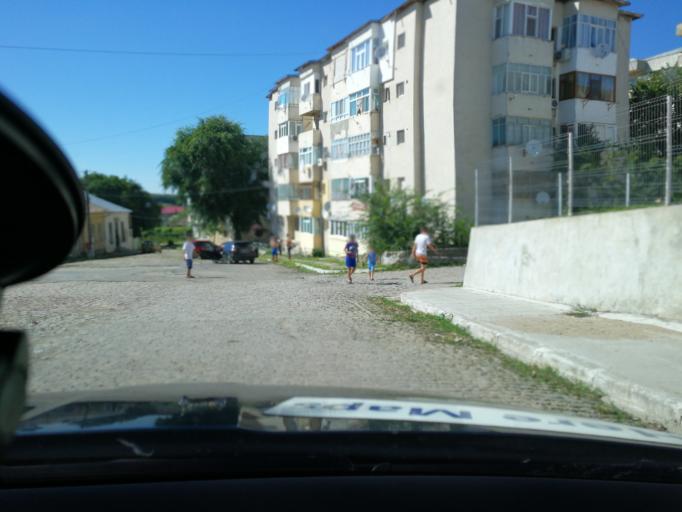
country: RO
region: Tulcea
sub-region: Oras Macin
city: Macin
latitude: 45.2450
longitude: 28.1295
